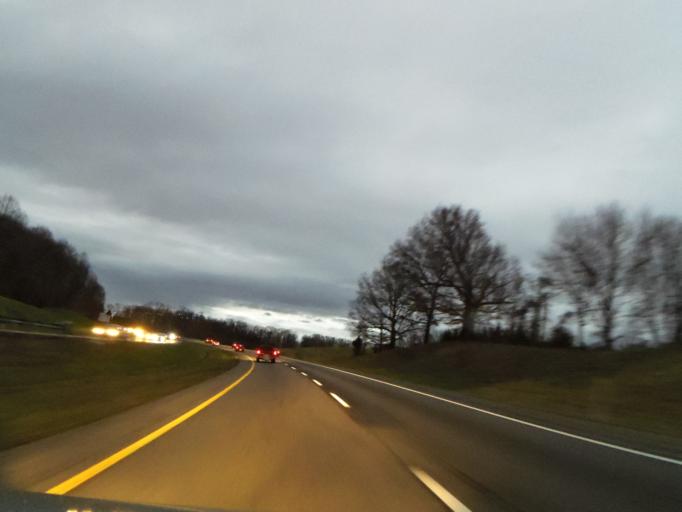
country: US
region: Tennessee
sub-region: Washington County
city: Oak Grove
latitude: 36.3945
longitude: -82.4486
